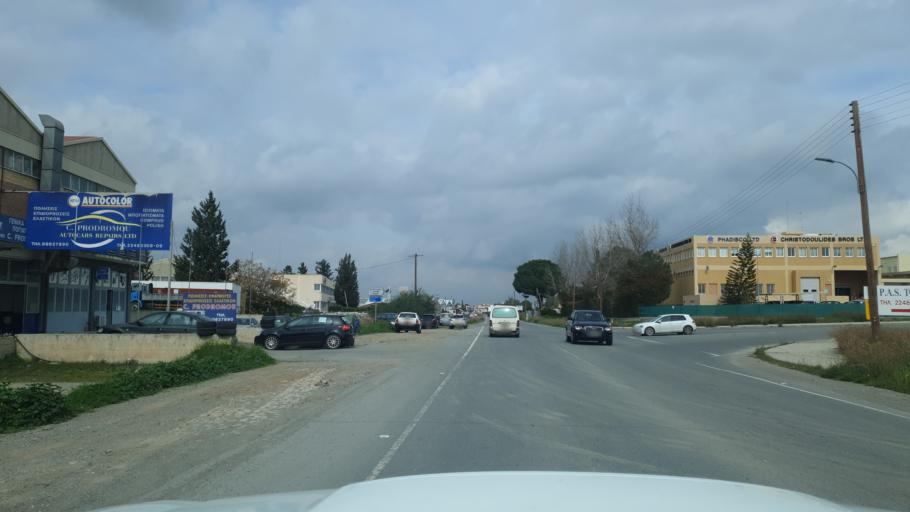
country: CY
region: Lefkosia
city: Geri
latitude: 35.0887
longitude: 33.3795
